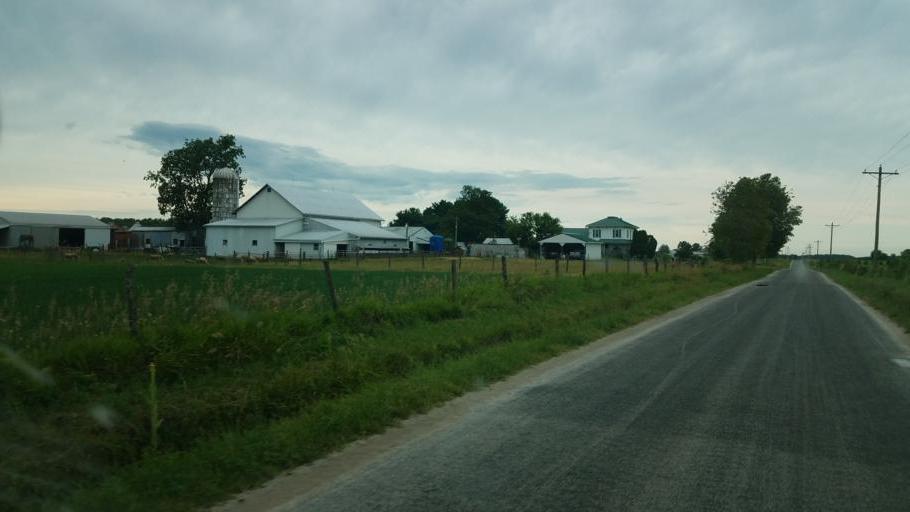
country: US
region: Ohio
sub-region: Ashland County
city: Ashland
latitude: 40.9408
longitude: -82.4073
